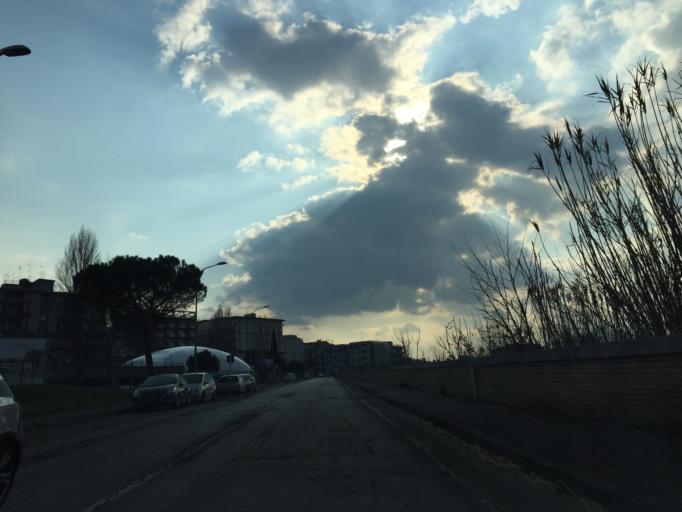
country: IT
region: Campania
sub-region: Provincia di Benevento
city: Benevento
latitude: 41.1350
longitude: 14.7767
